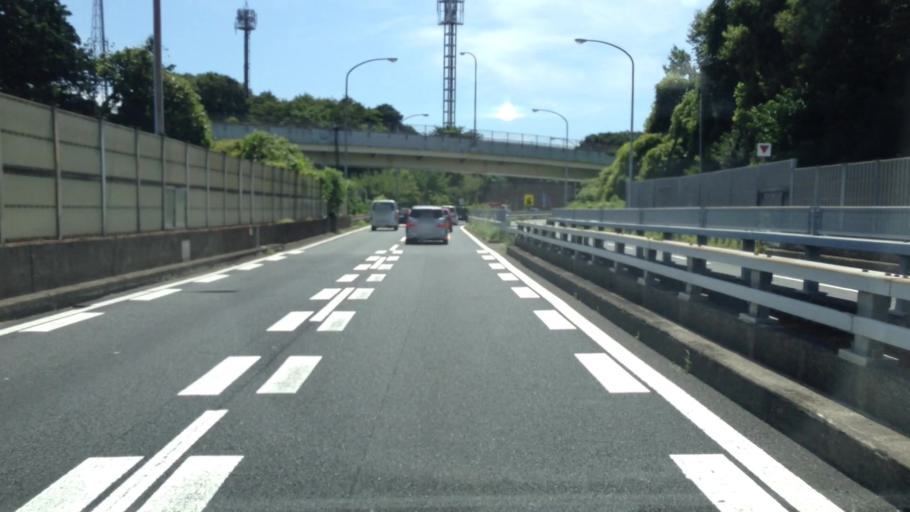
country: JP
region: Kanagawa
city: Yokohama
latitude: 35.4770
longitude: 139.5967
